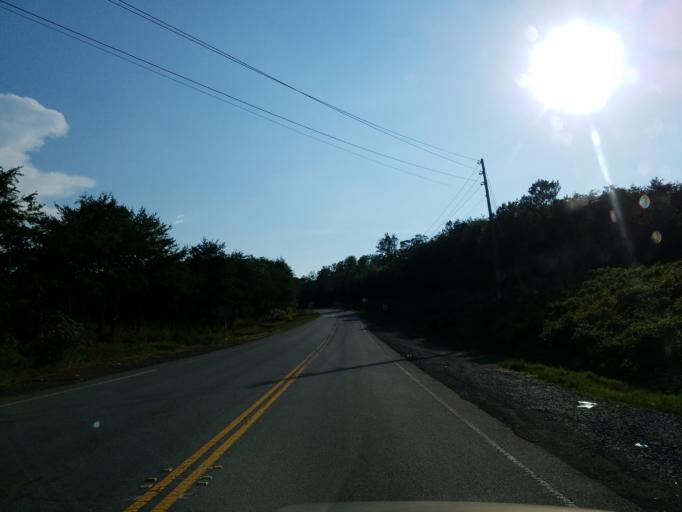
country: US
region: Georgia
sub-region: Bartow County
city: Rydal
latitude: 34.3427
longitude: -84.7189
